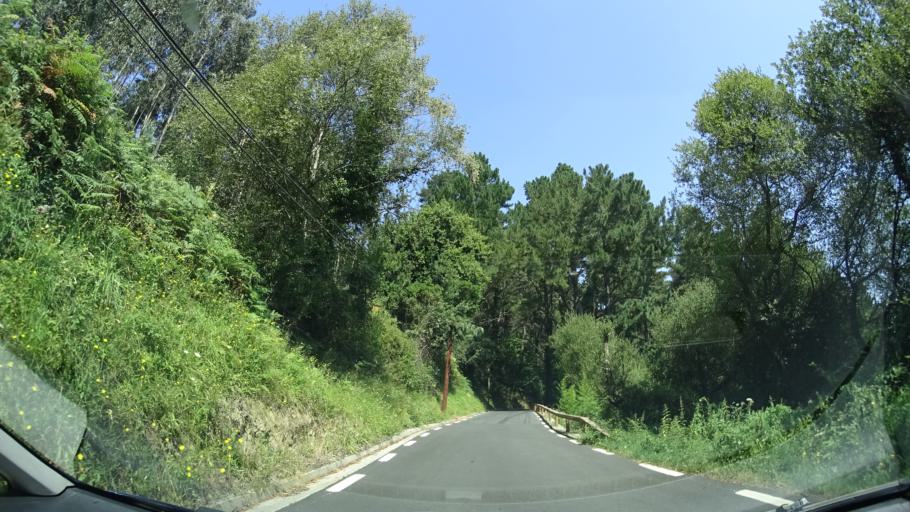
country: ES
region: Basque Country
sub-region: Bizkaia
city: Bermeo
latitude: 43.4357
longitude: -2.7476
